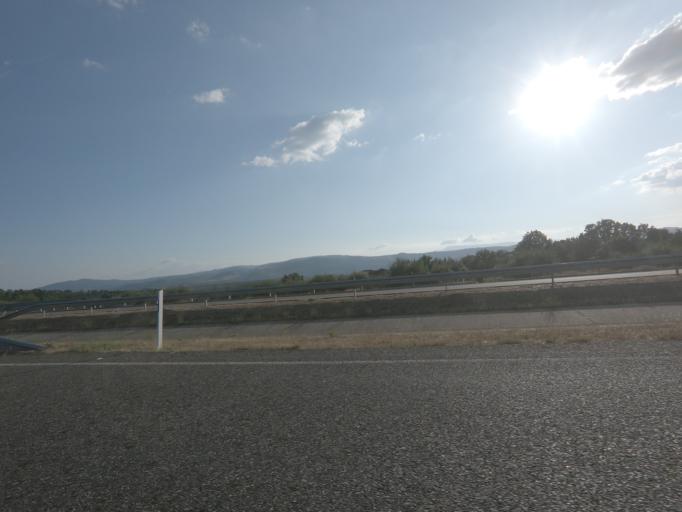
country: ES
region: Galicia
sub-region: Provincia de Ourense
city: Verin
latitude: 41.8966
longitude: -7.4243
